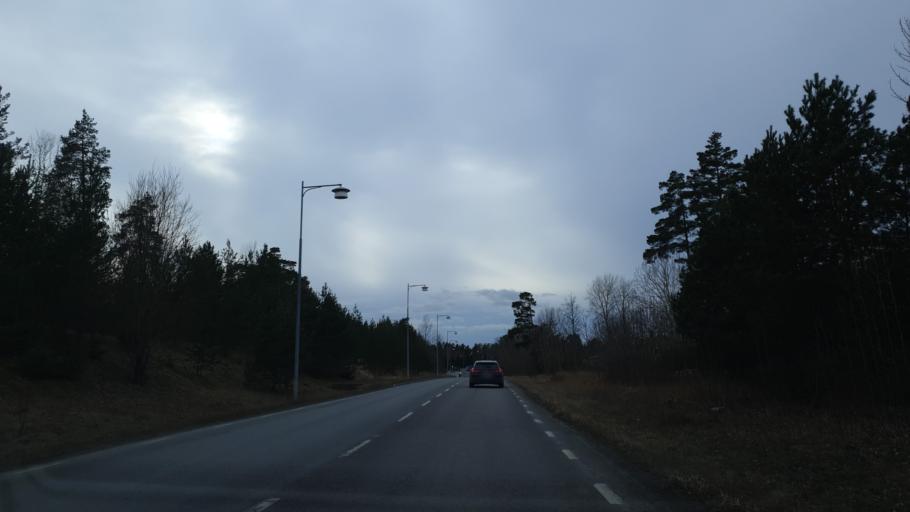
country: SE
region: Stockholm
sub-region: Vallentuna Kommun
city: Vallentuna
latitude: 59.5123
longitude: 18.0735
